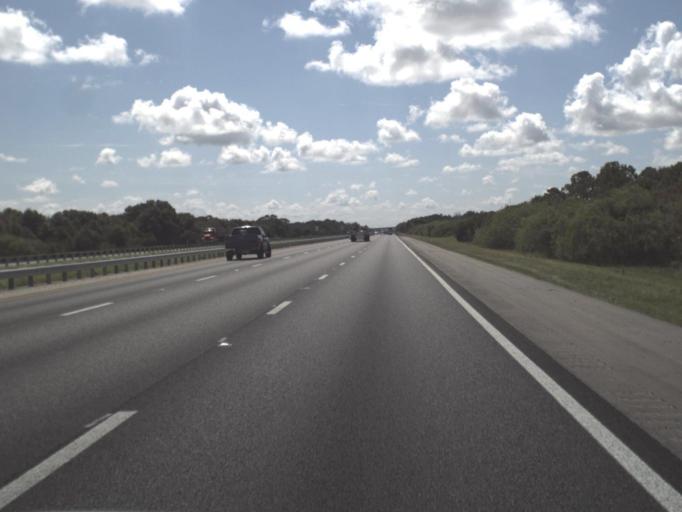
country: US
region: Florida
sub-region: Lee County
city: Suncoast Estates
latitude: 26.7512
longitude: -81.8640
